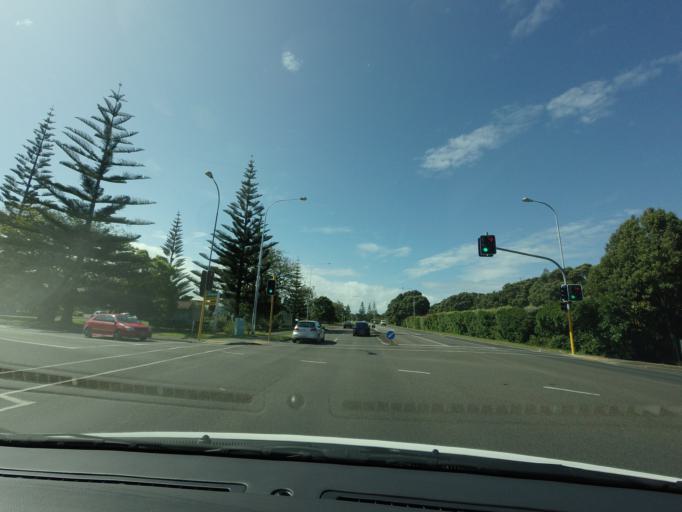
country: NZ
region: Auckland
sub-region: Auckland
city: Rothesay Bay
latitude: -36.5965
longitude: 174.6989
